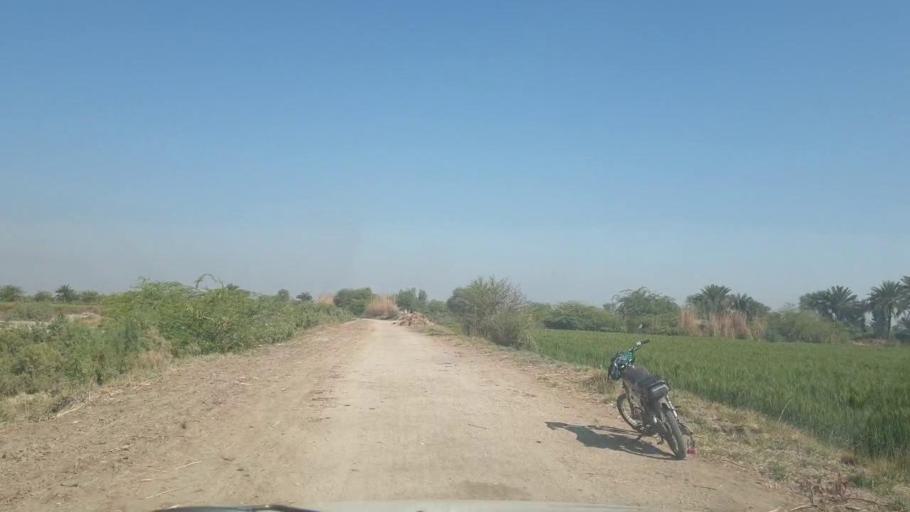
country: PK
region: Sindh
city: Mirpur Khas
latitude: 25.5142
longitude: 69.1623
